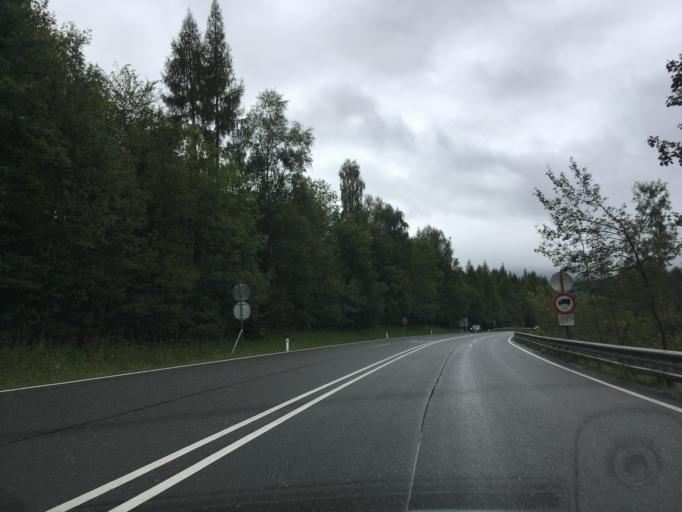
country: AT
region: Salzburg
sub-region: Politischer Bezirk Zell am See
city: Lend
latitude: 47.2943
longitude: 13.0503
